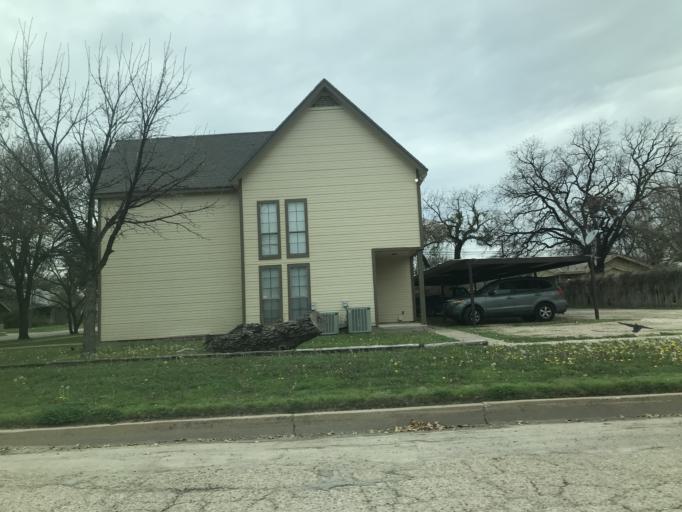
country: US
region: Texas
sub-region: Taylor County
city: Abilene
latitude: 32.4580
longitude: -99.7384
